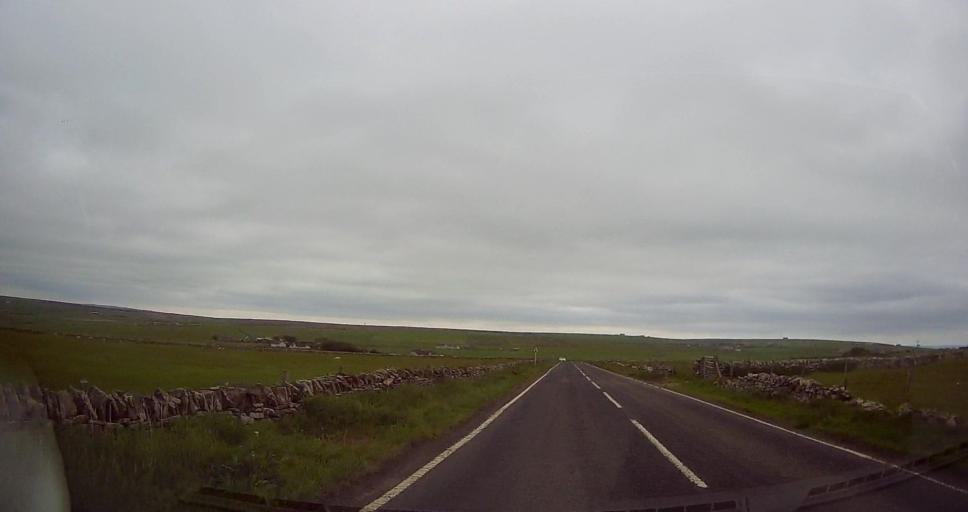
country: GB
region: Scotland
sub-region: Orkney Islands
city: Kirkwall
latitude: 58.9661
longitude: -2.9416
